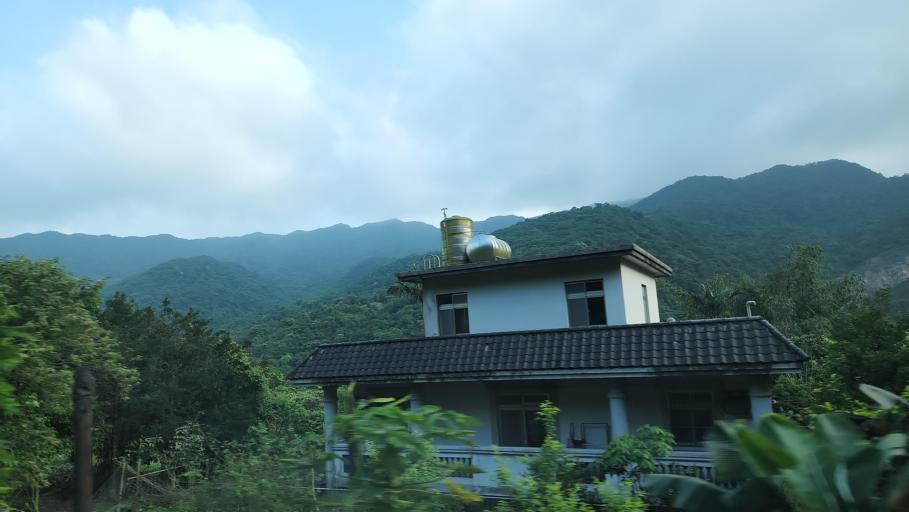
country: TW
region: Taiwan
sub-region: Keelung
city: Keelung
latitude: 25.1659
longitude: 121.6610
